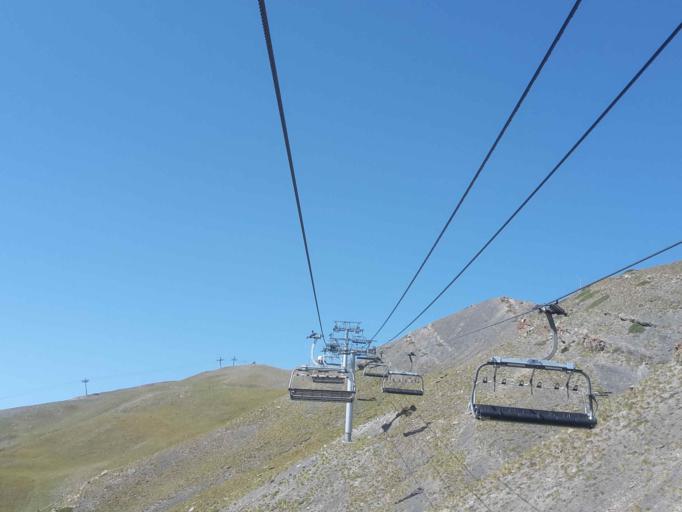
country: FR
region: Provence-Alpes-Cote d'Azur
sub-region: Departement des Hautes-Alpes
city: Guillestre
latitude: 44.5890
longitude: 6.6604
